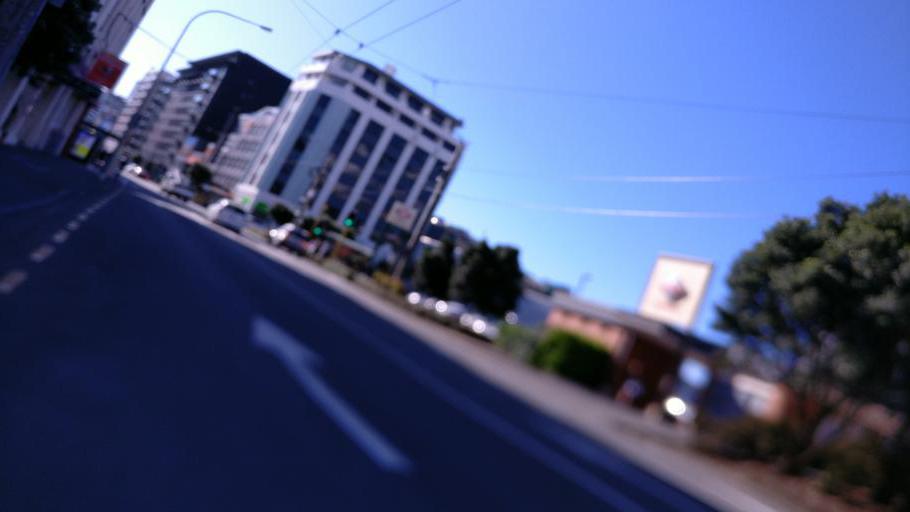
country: NZ
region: Wellington
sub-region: Wellington City
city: Wellington
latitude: -41.2931
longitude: 174.7842
